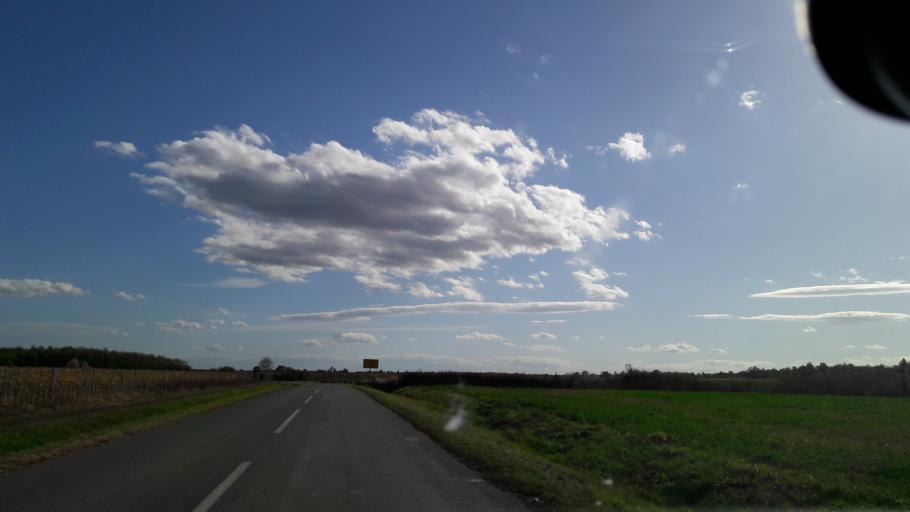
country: HR
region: Osjecko-Baranjska
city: Gorjani
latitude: 45.3825
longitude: 18.2536
